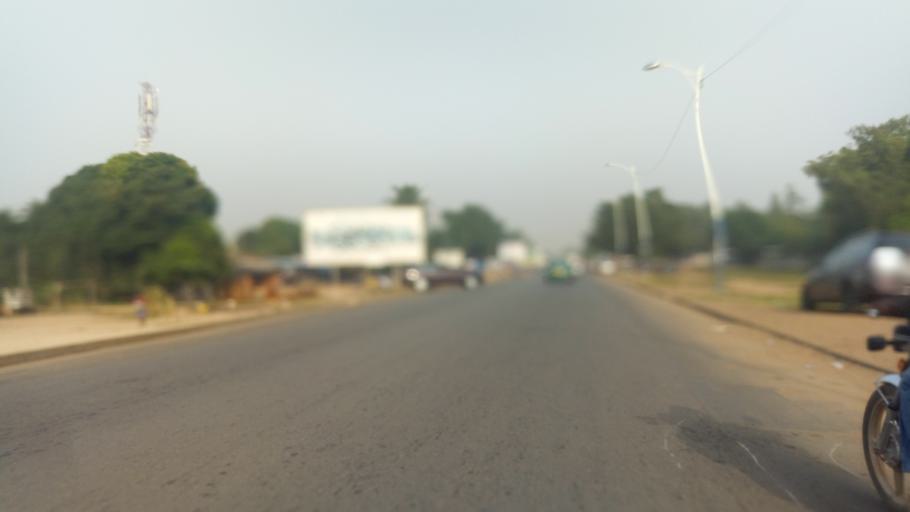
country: TG
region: Maritime
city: Lome
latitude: 6.1895
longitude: 1.1617
